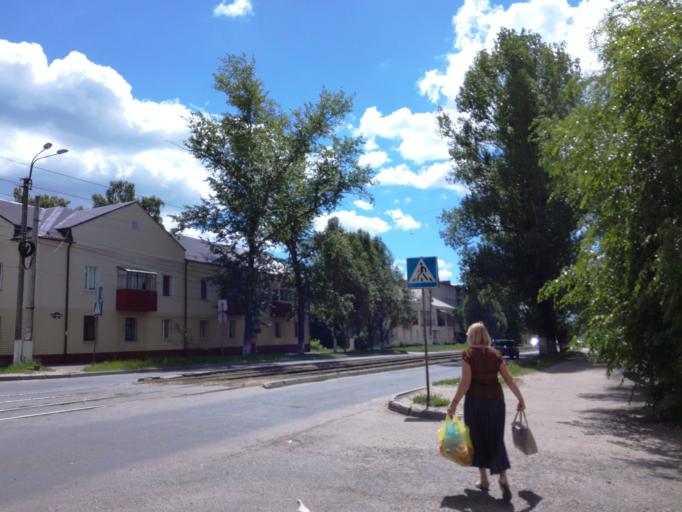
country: RU
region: Kursk
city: Kursk
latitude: 51.7445
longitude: 36.2464
